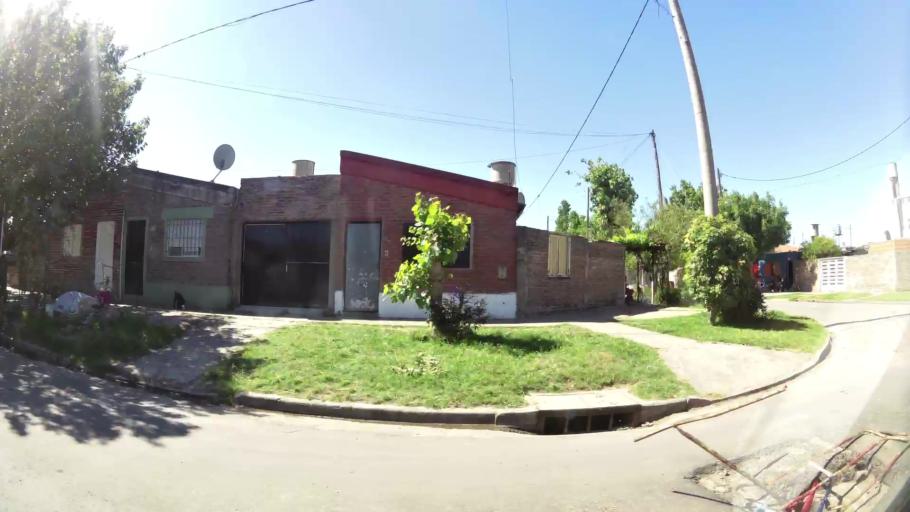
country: AR
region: Santa Fe
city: Granadero Baigorria
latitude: -32.9258
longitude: -60.7064
